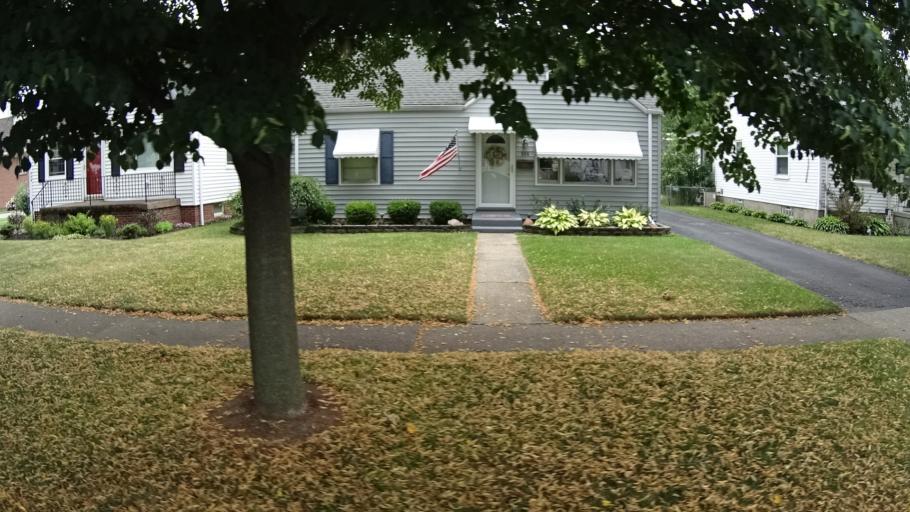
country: US
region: Ohio
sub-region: Erie County
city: Sandusky
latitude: 41.4371
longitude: -82.6941
